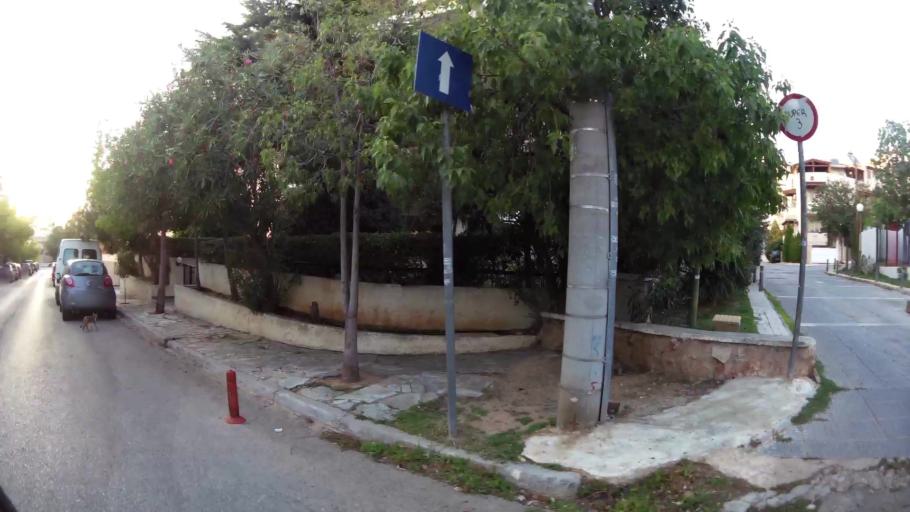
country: GR
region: Attica
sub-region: Nomarchia Athinas
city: Glyfada
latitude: 37.8805
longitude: 23.7648
